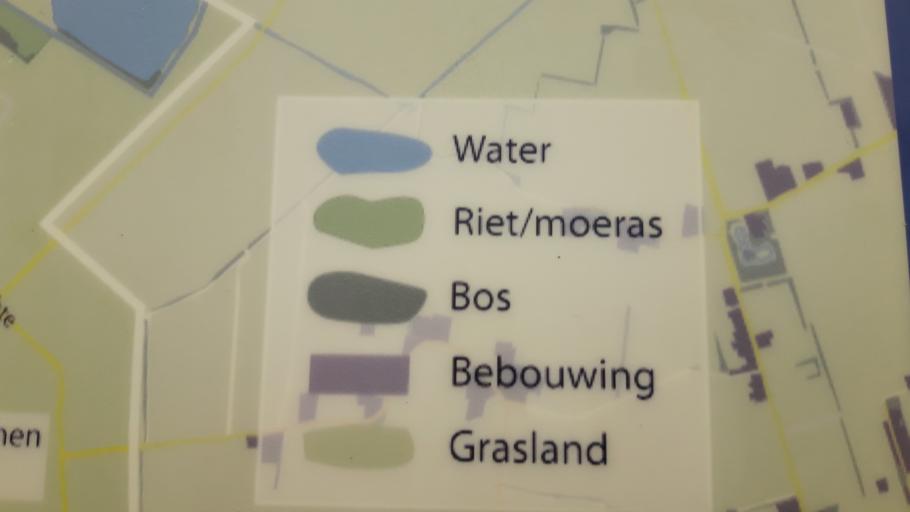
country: NL
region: Friesland
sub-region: Gemeente Boarnsterhim
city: Warten
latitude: 53.1159
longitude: 5.8858
